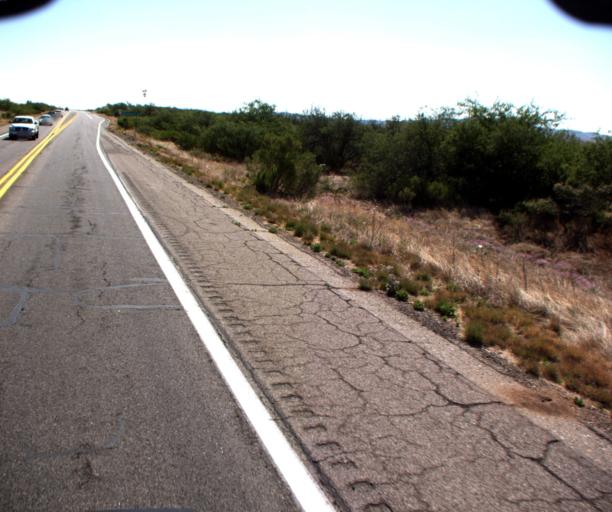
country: US
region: Arizona
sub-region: Pinal County
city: Oracle
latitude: 32.6034
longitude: -110.8645
